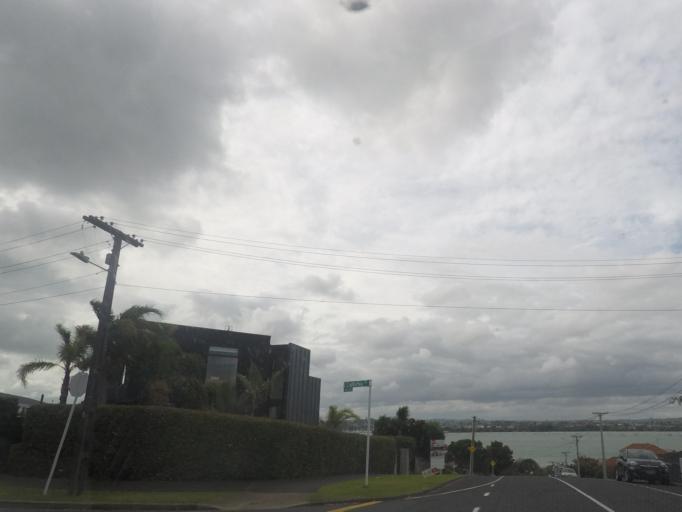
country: NZ
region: Auckland
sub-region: Auckland
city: Tamaki
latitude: -36.8710
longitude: 174.8807
